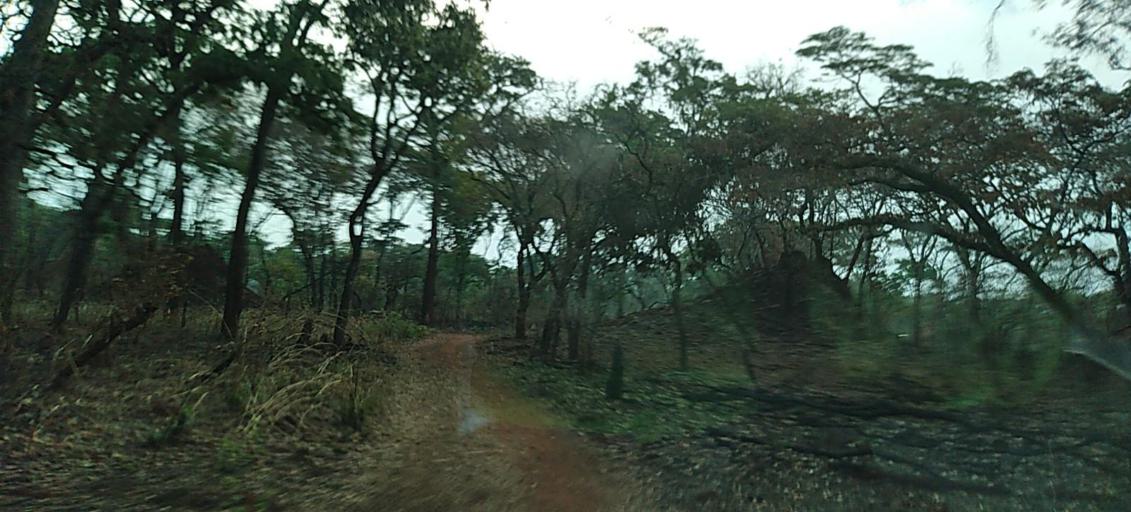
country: ZM
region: North-Western
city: Solwezi
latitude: -12.0446
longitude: 26.0106
